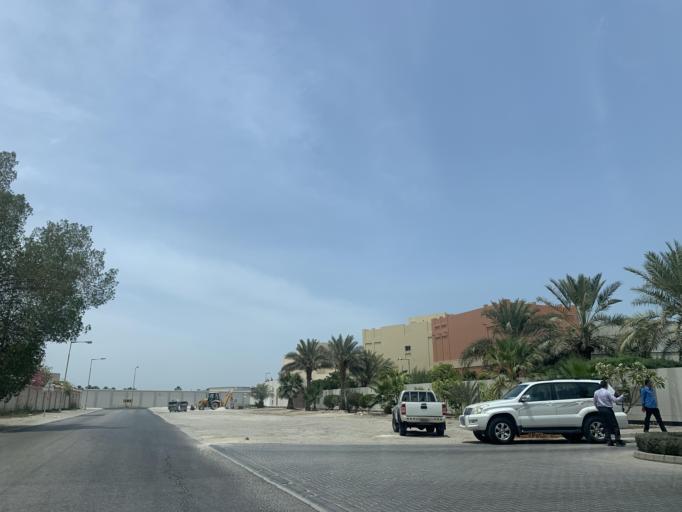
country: BH
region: Central Governorate
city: Madinat Hamad
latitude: 26.1811
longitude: 50.4679
